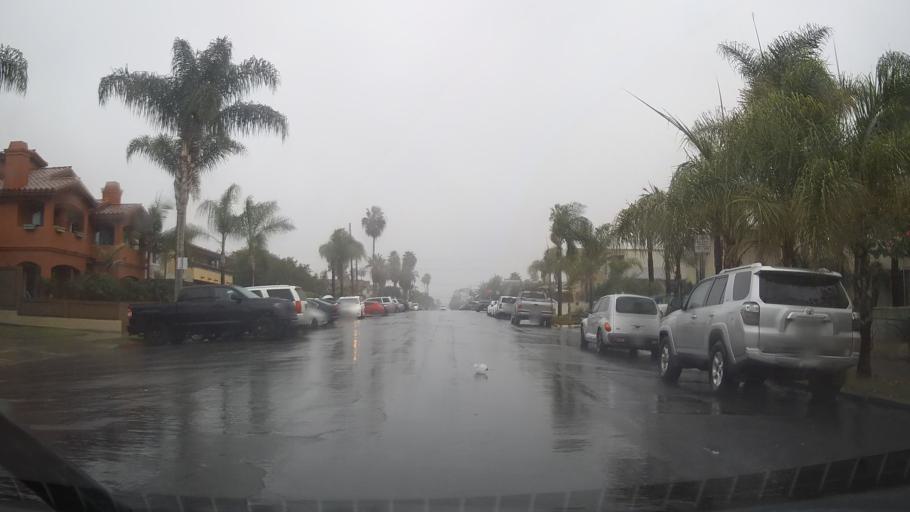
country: US
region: California
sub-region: San Diego County
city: San Diego
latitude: 32.7491
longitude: -117.1375
